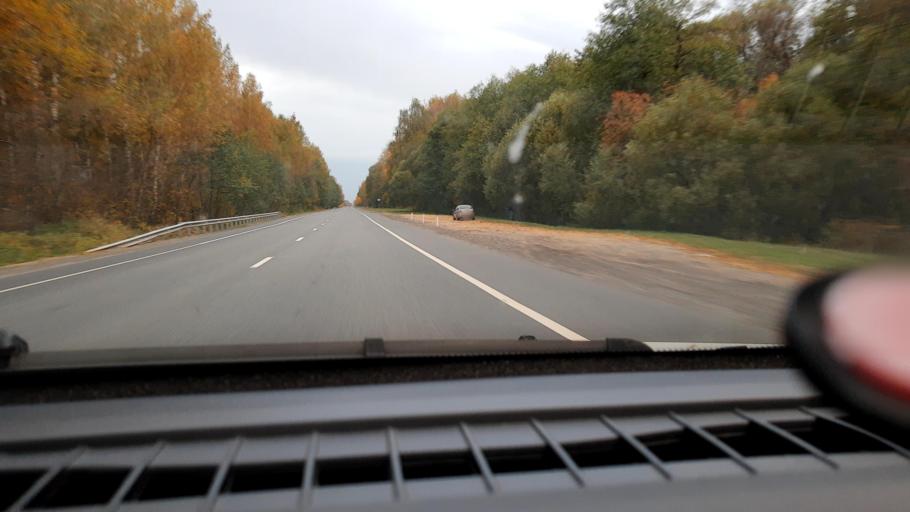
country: RU
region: Vladimir
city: Orgtrud
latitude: 56.2014
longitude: 40.7905
